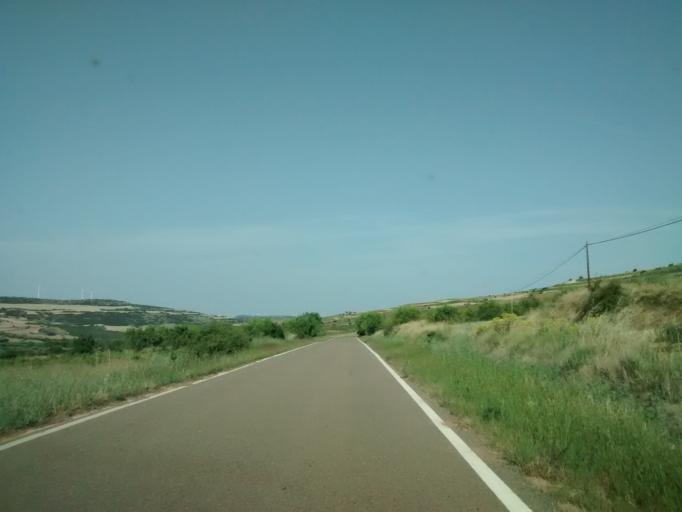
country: ES
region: Aragon
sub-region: Provincia de Zaragoza
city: Trasmoz
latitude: 41.8405
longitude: -1.7366
